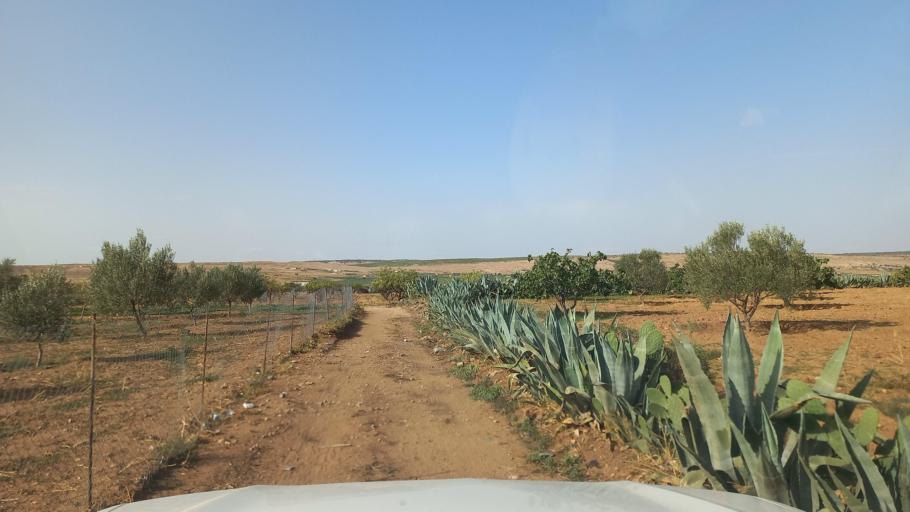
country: TN
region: Al Qasrayn
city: Kasserine
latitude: 35.3444
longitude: 8.8480
